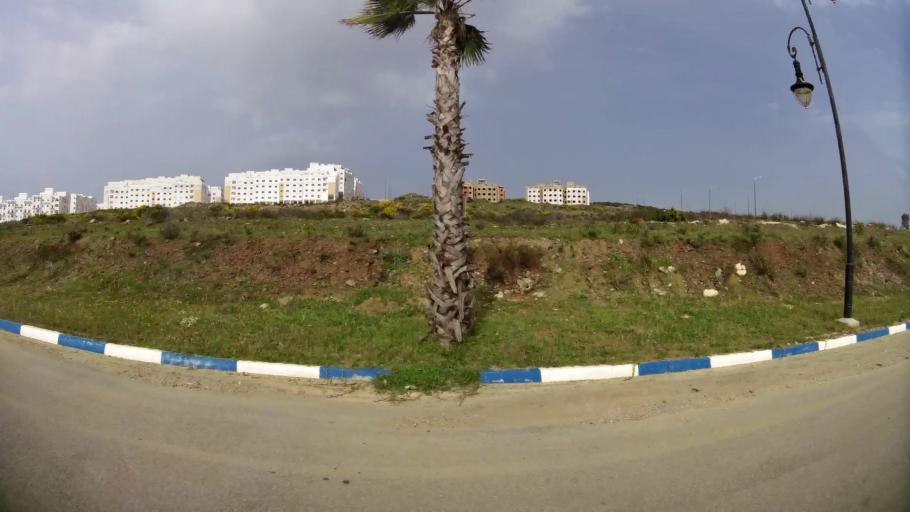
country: MA
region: Tanger-Tetouan
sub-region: Tanger-Assilah
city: Boukhalef
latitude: 35.7008
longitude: -5.9324
